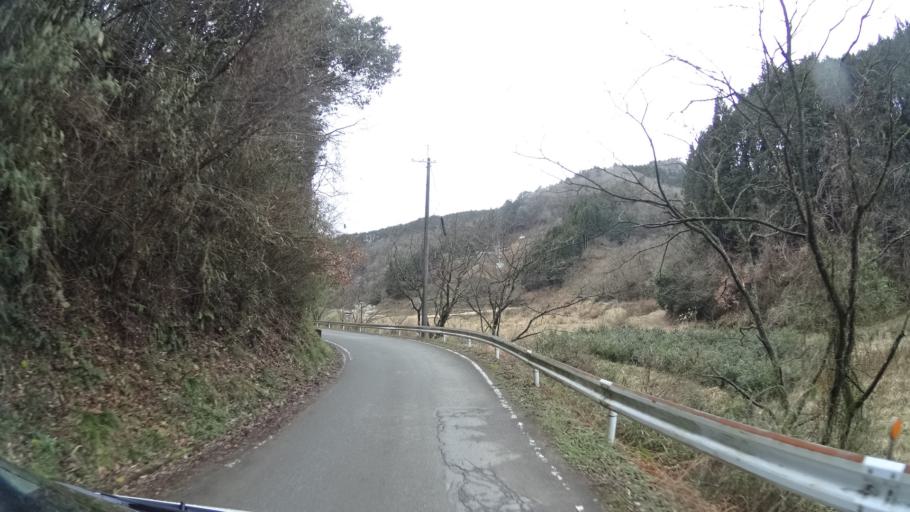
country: JP
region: Kyoto
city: Maizuru
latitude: 35.3460
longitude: 135.3494
